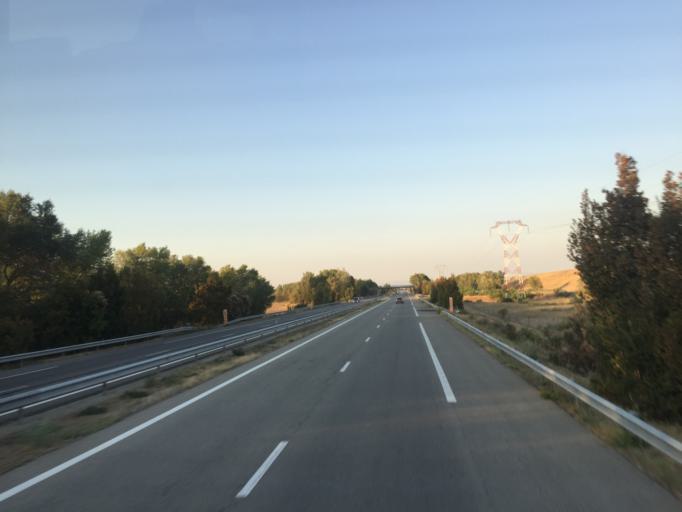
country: FR
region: Provence-Alpes-Cote d'Azur
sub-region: Departement des Alpes-de-Haute-Provence
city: Sainte-Tulle
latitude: 43.7411
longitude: 5.7570
